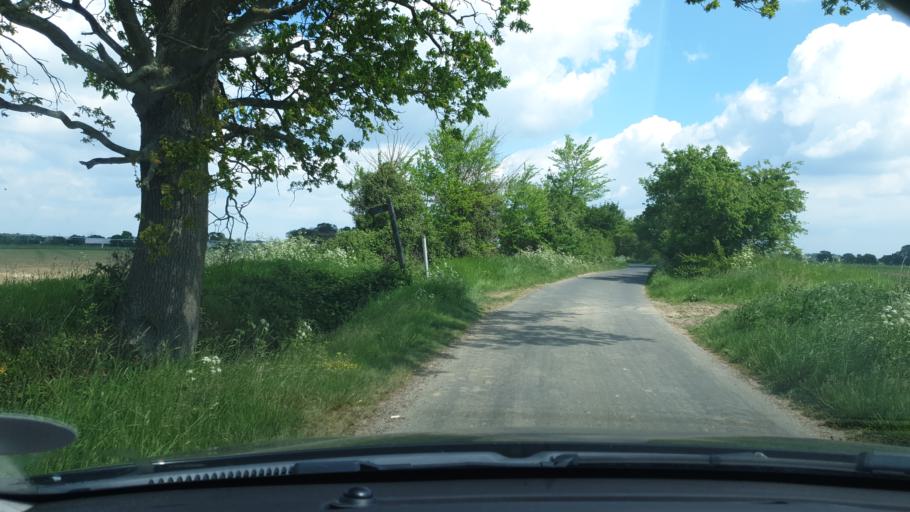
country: GB
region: England
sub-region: Essex
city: Great Bentley
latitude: 51.8444
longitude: 1.0748
